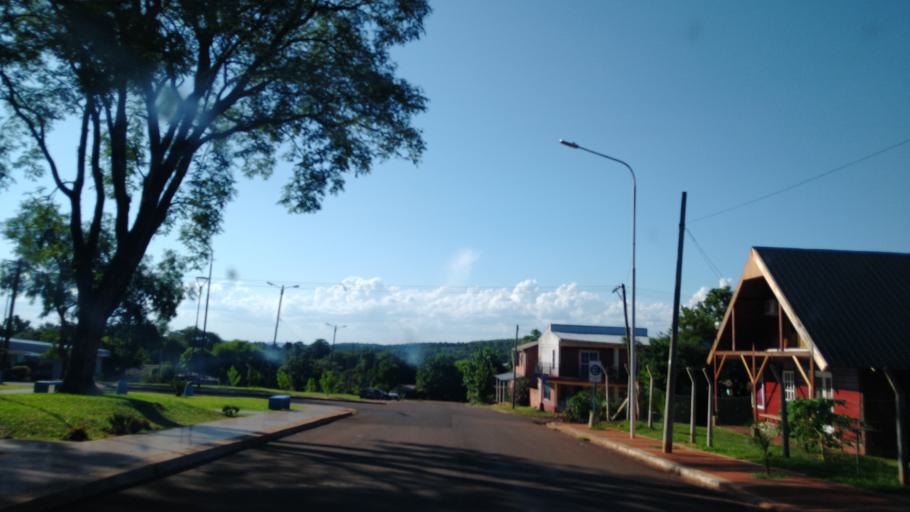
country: AR
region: Misiones
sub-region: Departamento de San Ignacio
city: San Ignacio
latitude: -27.2522
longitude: -55.5339
